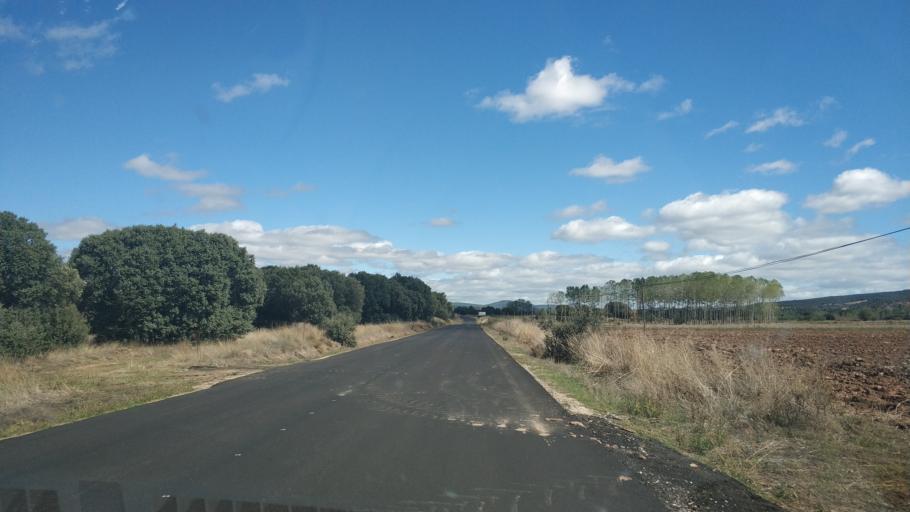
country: ES
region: Castille and Leon
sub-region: Provincia de Burgos
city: Puentedura
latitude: 42.0356
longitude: -3.6046
